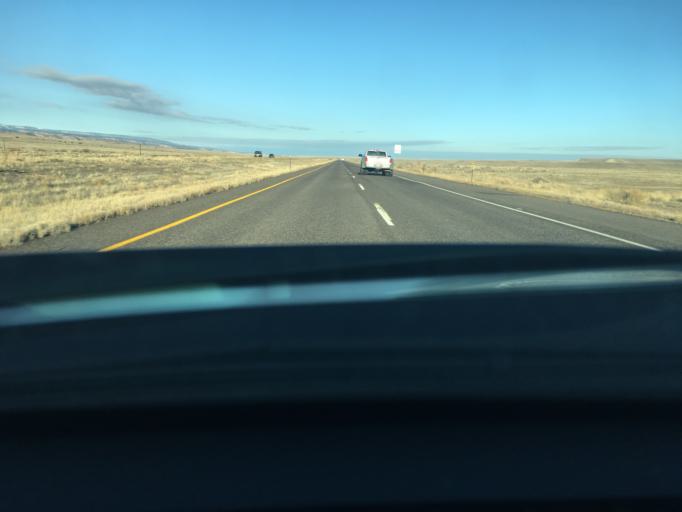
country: US
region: Colorado
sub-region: Delta County
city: Delta
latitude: 38.7897
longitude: -108.2535
